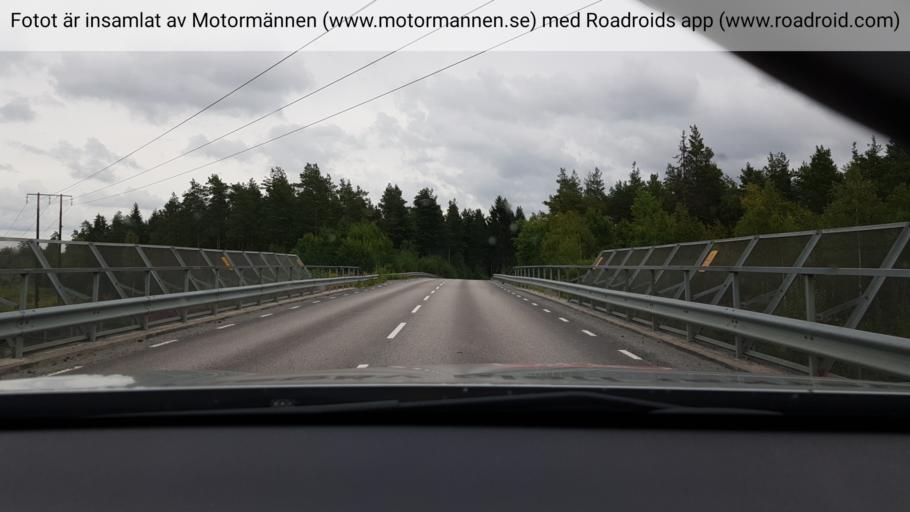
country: SE
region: Stockholm
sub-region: Sigtuna Kommun
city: Rosersberg
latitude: 59.6216
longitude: 17.9200
